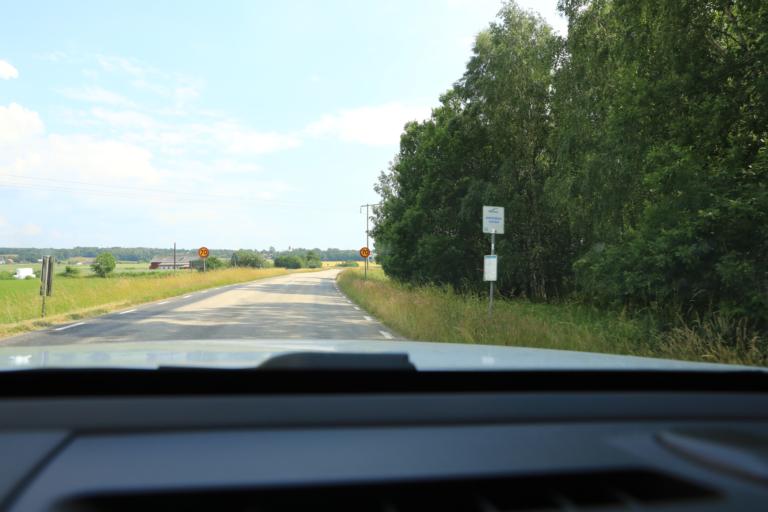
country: SE
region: Halland
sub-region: Varbergs Kommun
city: Varberg
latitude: 57.1708
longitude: 12.2995
